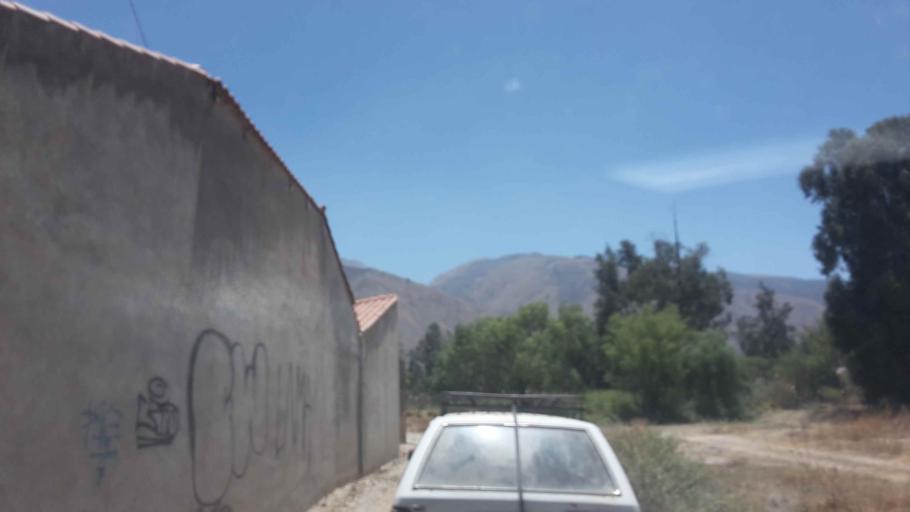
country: BO
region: Cochabamba
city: Cochabamba
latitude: -17.3447
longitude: -66.2148
